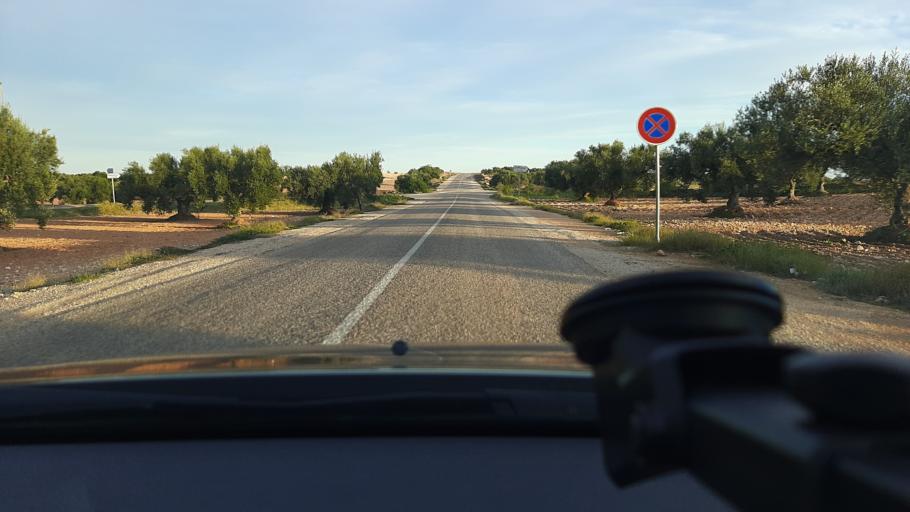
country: TN
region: Safaqis
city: Sfax
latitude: 34.9565
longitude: 10.5442
